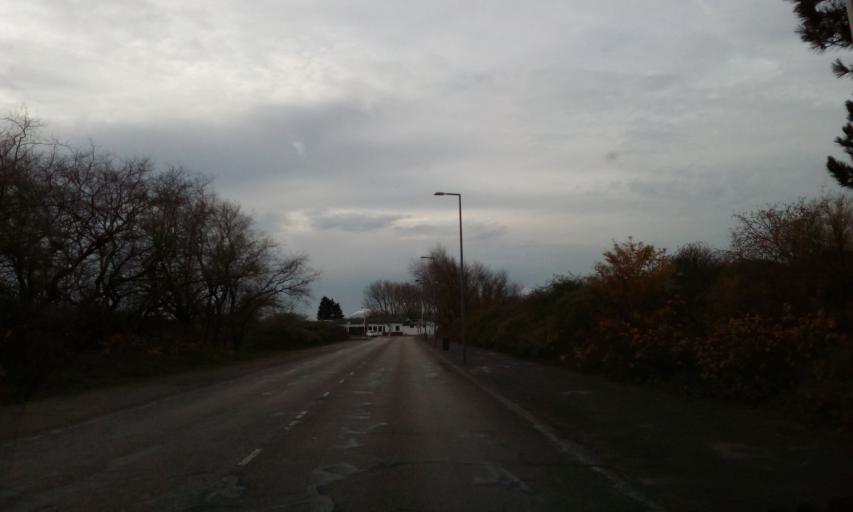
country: NL
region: South Holland
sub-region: Gemeente Rotterdam
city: Hoek van Holland
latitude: 51.9848
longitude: 4.1140
